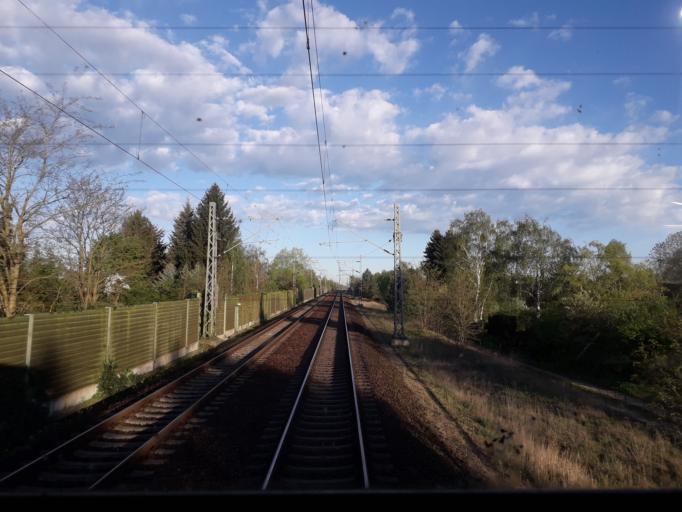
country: DE
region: Berlin
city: Falkenhagener Feld
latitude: 52.5402
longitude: 13.1648
